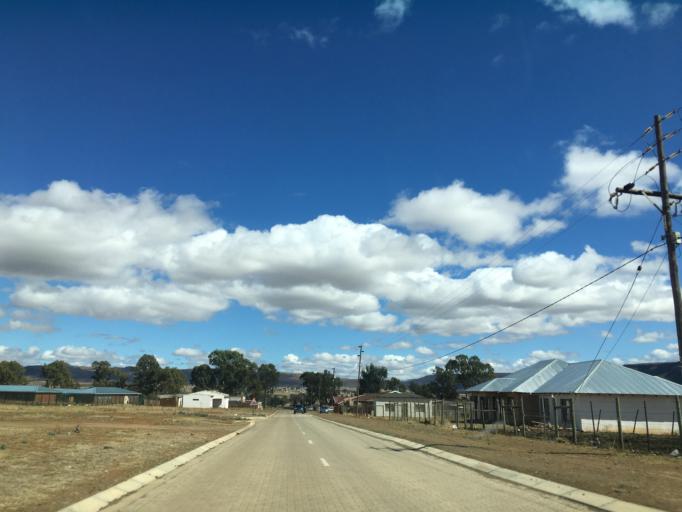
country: ZA
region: Eastern Cape
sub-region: Chris Hani District Municipality
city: Cala
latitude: -31.5349
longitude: 27.6919
